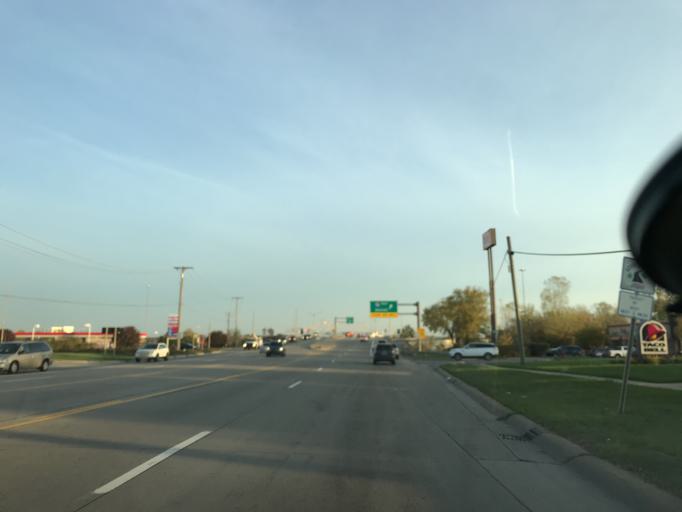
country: US
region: Michigan
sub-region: Oakland County
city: Wixom
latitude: 42.4949
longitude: -83.5358
